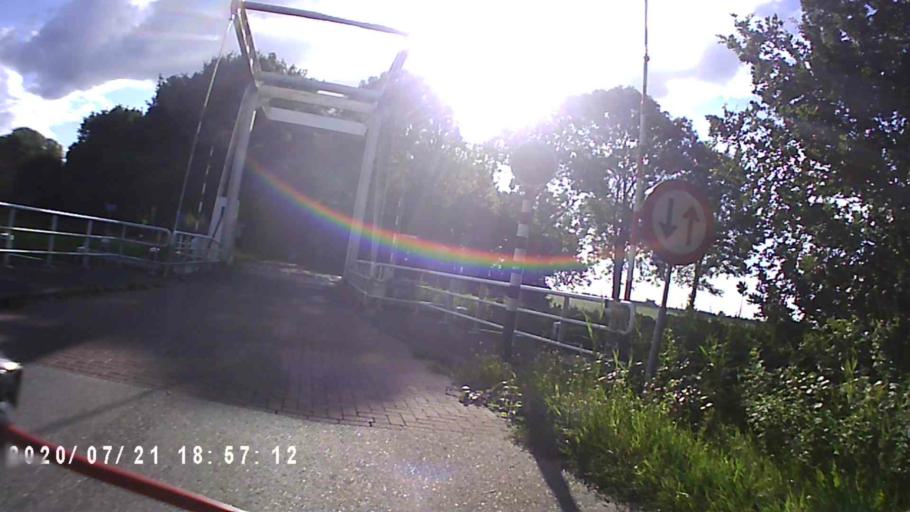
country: NL
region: Groningen
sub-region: Gemeente Hoogezand-Sappemeer
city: Hoogezand
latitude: 53.2179
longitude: 6.7389
